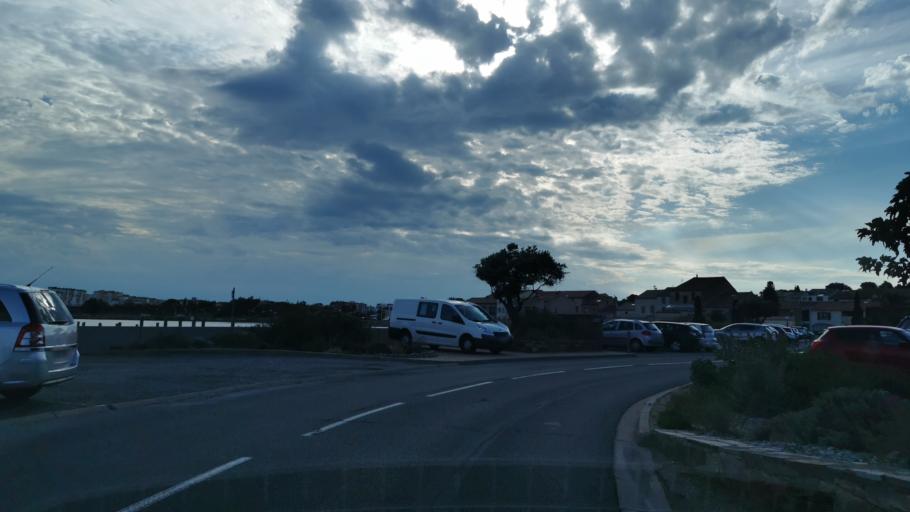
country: FR
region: Languedoc-Roussillon
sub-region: Departement de l'Aude
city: Gruissan
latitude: 43.1086
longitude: 3.0866
